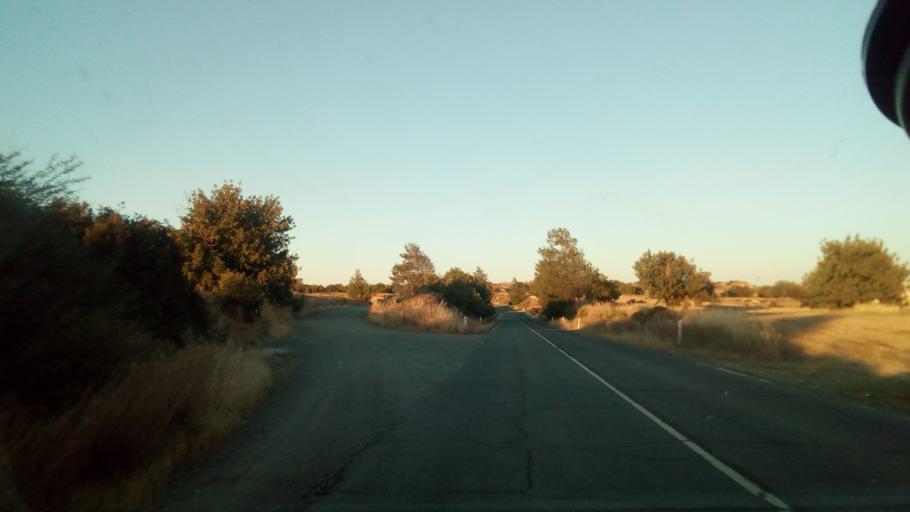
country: CY
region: Larnaka
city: Kofinou
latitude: 34.8389
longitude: 33.4230
